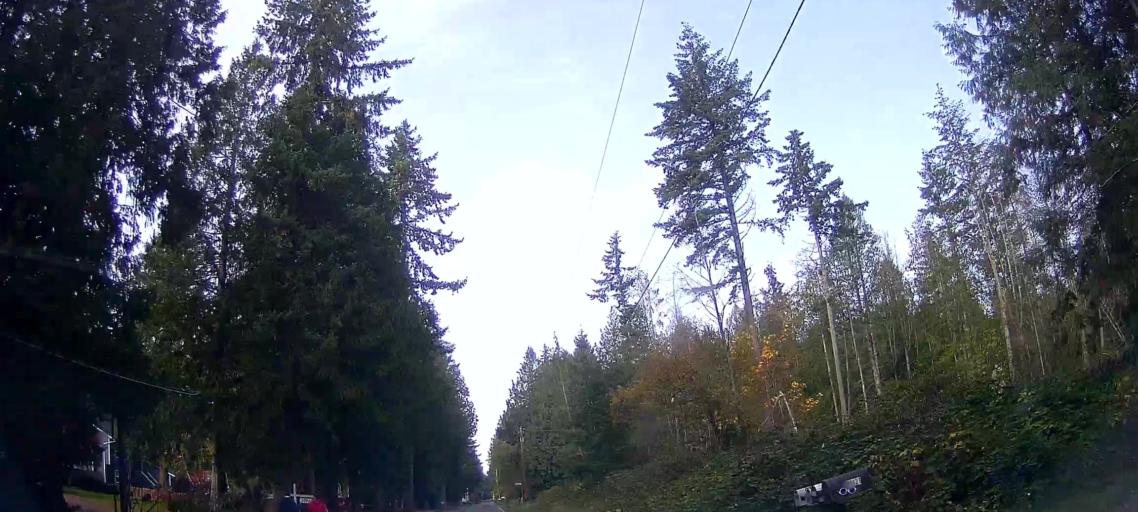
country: US
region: Washington
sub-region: Snohomish County
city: Stanwood
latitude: 48.2813
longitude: -122.3364
